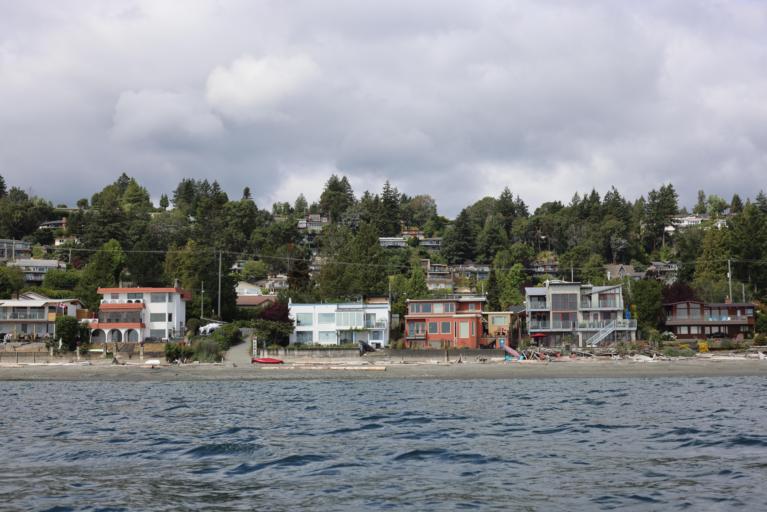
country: CA
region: British Columbia
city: Victoria
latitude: 48.5198
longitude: -123.3646
